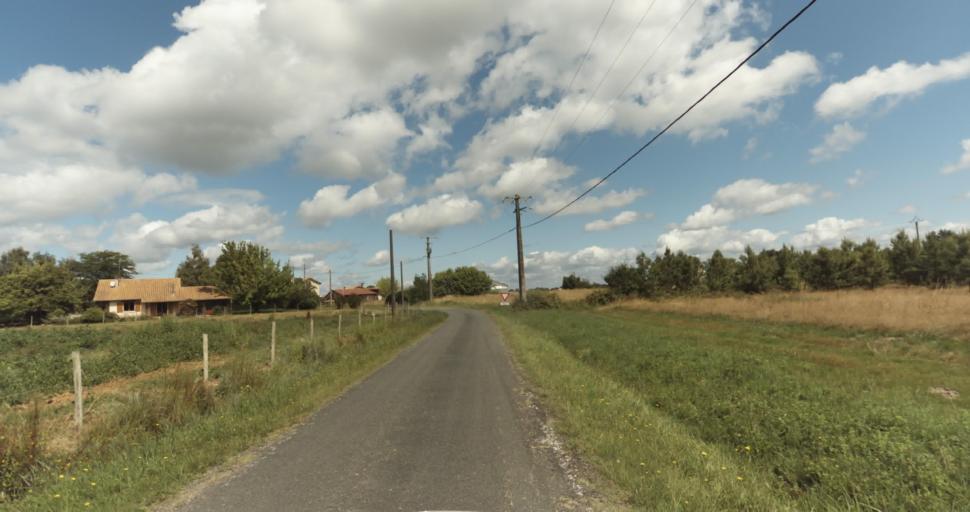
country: FR
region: Aquitaine
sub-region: Departement de la Gironde
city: Bazas
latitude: 44.4619
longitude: -0.1836
